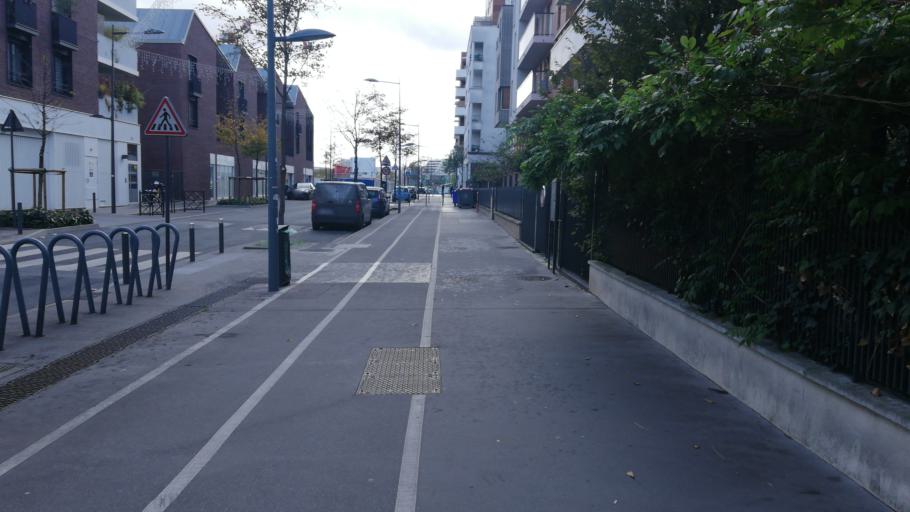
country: FR
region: Ile-de-France
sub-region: Departement des Hauts-de-Seine
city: Villeneuve-la-Garenne
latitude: 48.9192
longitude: 2.3166
